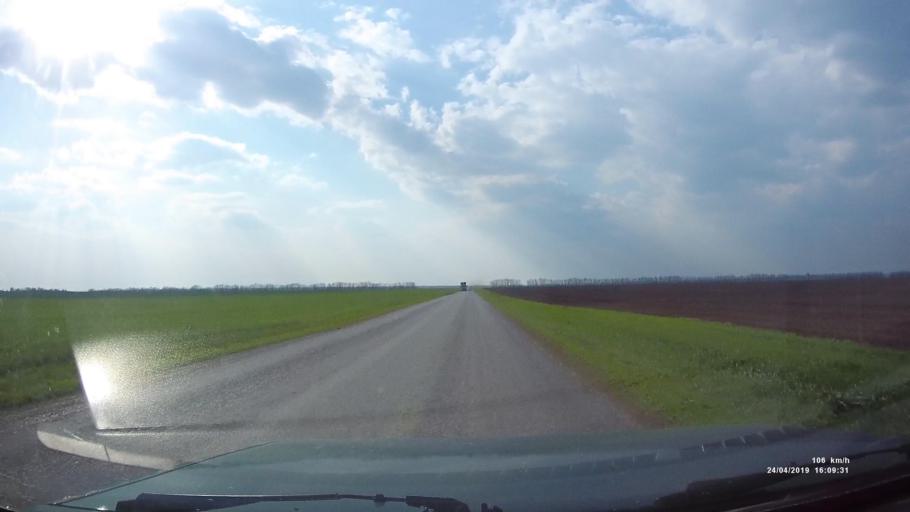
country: RU
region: Rostov
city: Sovetskoye
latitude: 46.7087
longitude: 42.2881
